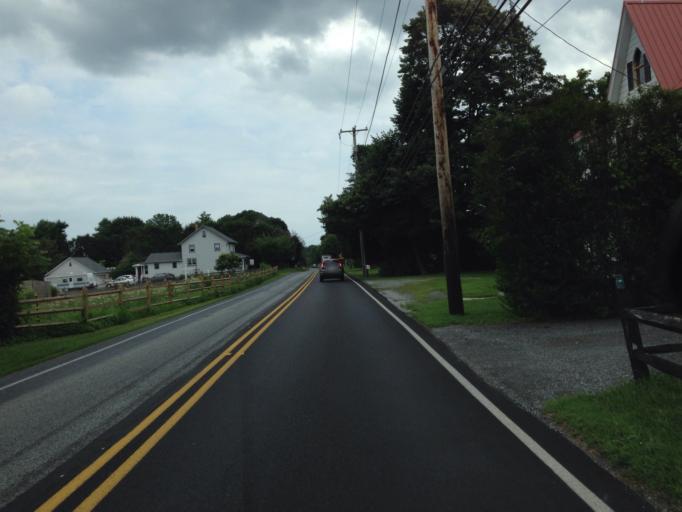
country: US
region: Pennsylvania
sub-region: Chester County
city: West Grove
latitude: 39.7812
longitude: -75.8740
